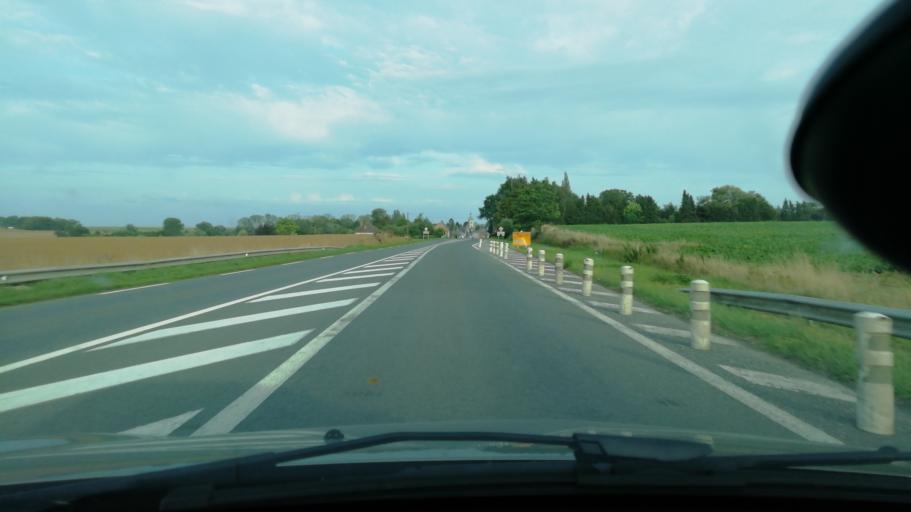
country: FR
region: Nord-Pas-de-Calais
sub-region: Departement du Nord
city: Viesly
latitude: 50.1261
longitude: 3.4464
